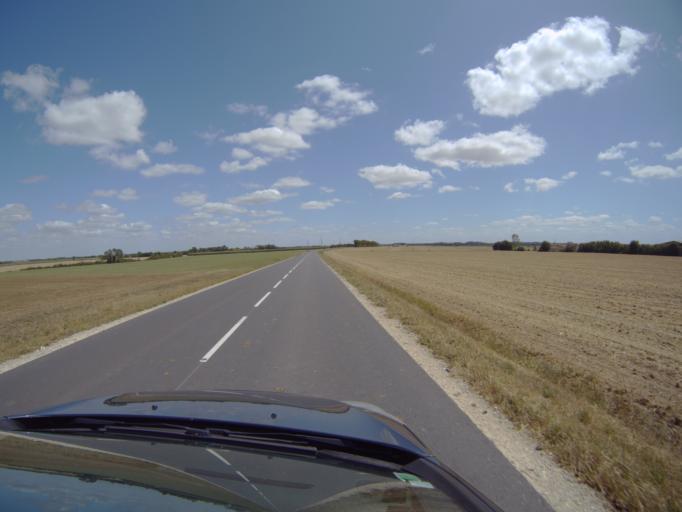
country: FR
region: Poitou-Charentes
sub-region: Departement de la Charente-Maritime
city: Saint-Jean-de-Liversay
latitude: 46.2843
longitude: -0.9263
